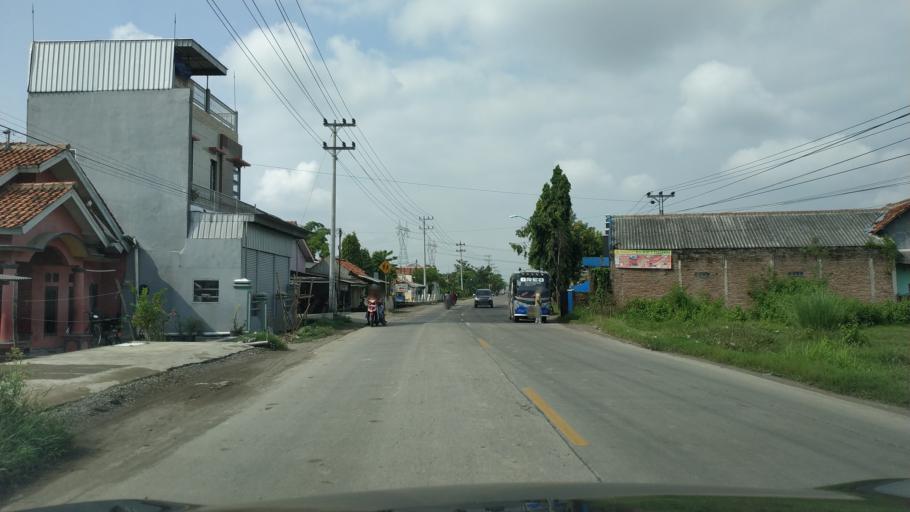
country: ID
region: Central Java
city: Ketanggungan
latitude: -6.9067
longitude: 108.8890
